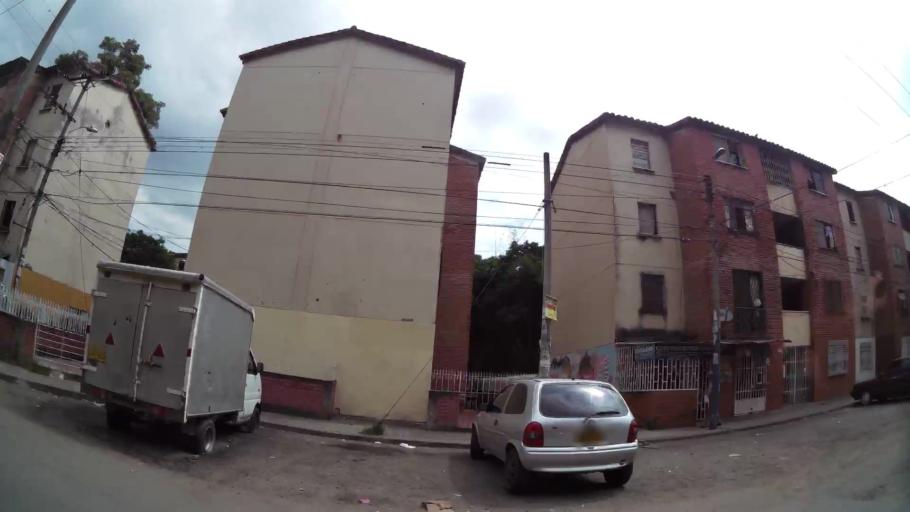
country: CO
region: Valle del Cauca
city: Cali
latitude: 3.4875
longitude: -76.4925
